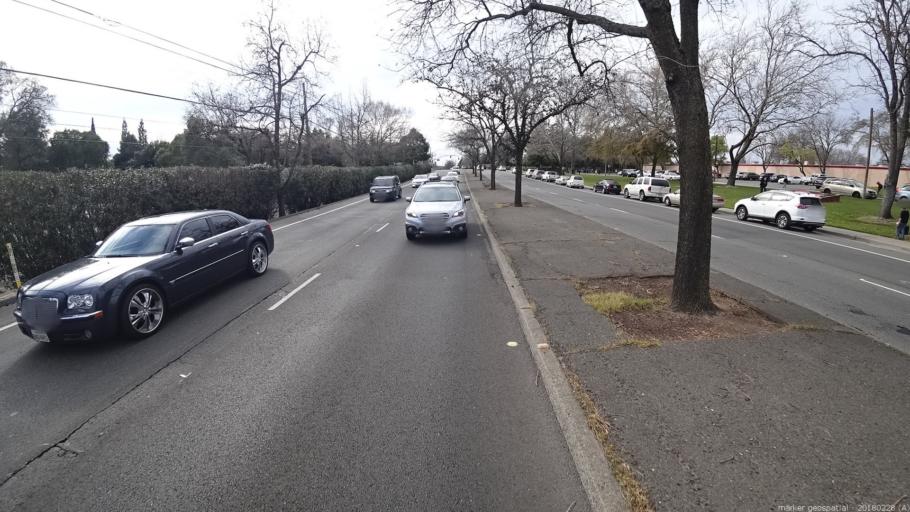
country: US
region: California
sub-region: Sacramento County
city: Fair Oaks
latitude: 38.6642
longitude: -121.2517
